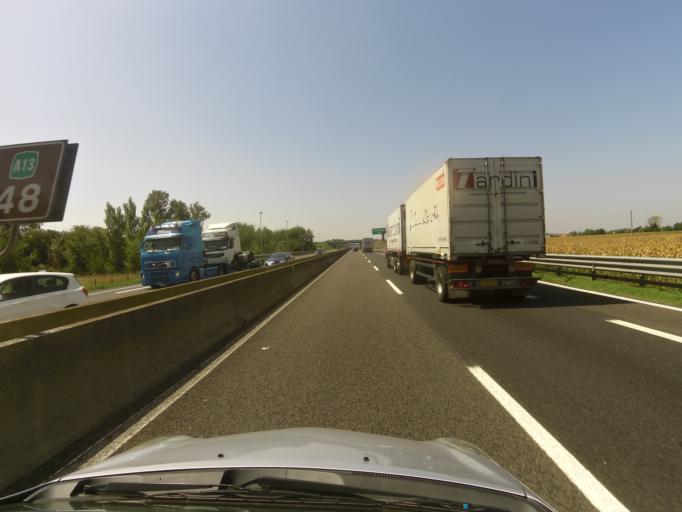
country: IT
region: Veneto
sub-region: Provincia di Rovigo
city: Occhiobello
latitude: 44.9263
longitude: 11.5966
